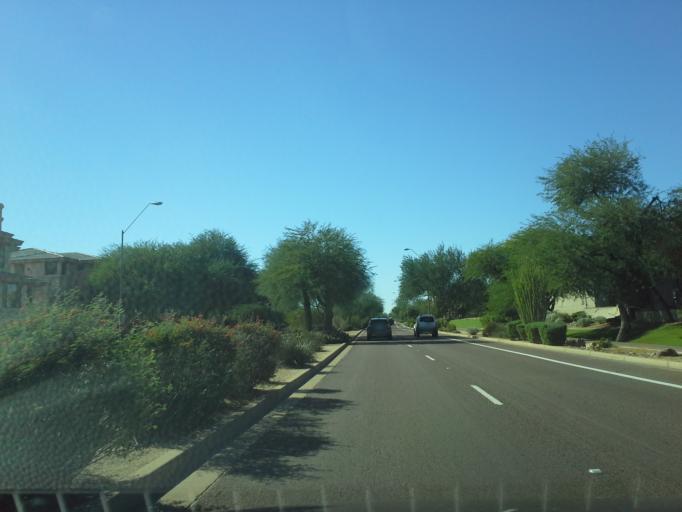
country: US
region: Arizona
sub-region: Maricopa County
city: Paradise Valley
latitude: 33.6402
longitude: -111.8976
